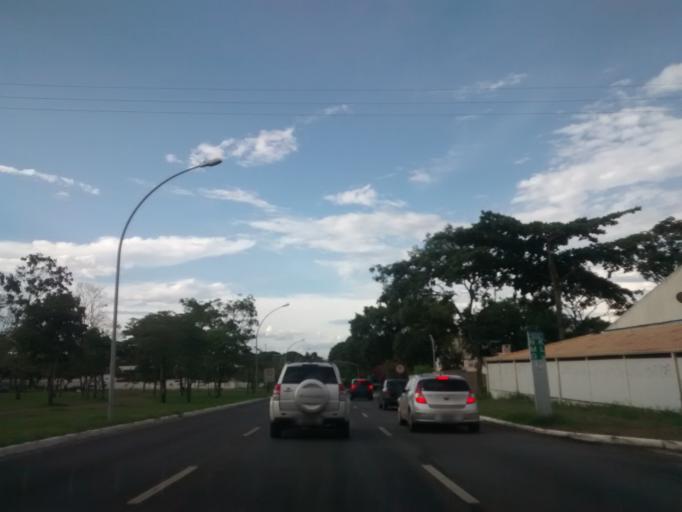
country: BR
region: Federal District
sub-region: Brasilia
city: Brasilia
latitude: -15.7596
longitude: -47.8954
